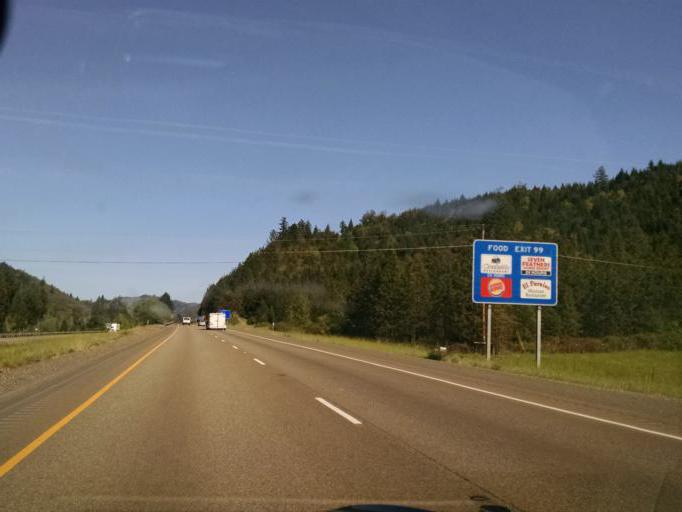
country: US
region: Oregon
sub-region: Douglas County
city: Canyonville
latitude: 42.9478
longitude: -123.3059
